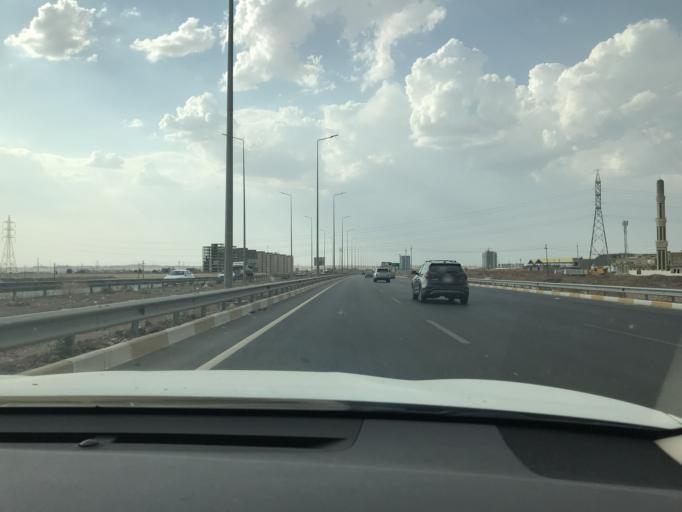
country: IQ
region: Arbil
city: Erbil
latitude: 36.1613
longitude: 43.9568
